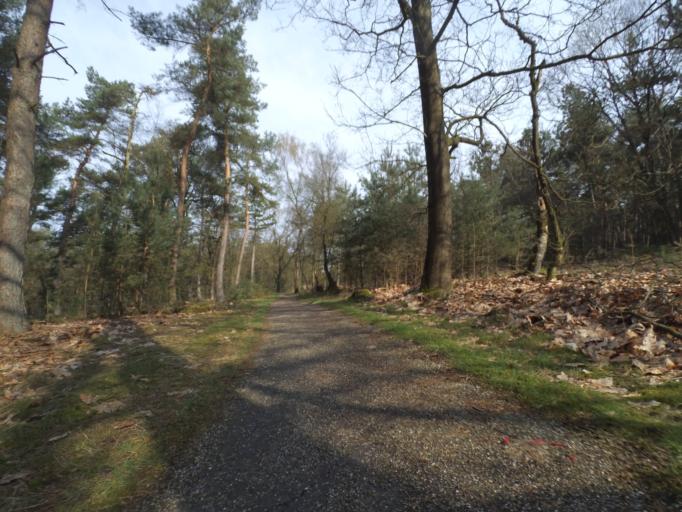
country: NL
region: Gelderland
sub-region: Gemeente Ede
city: Harskamp
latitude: 52.1547
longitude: 5.7379
